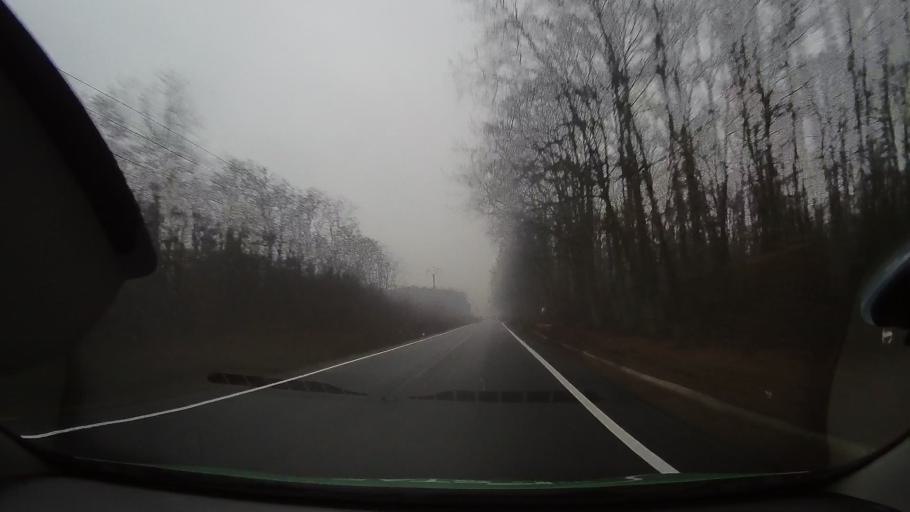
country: RO
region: Bihor
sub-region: Comuna Olcea
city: Olcea
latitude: 46.6993
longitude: 21.9647
